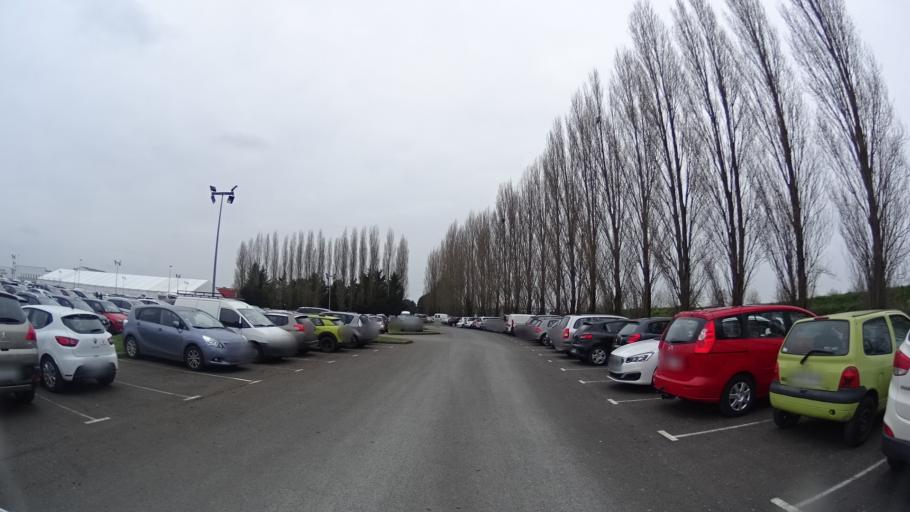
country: FR
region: Brittany
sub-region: Departement d'Ille-et-Vilaine
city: Saint-Jacques-de-la-Lande
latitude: 48.0584
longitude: -1.7283
